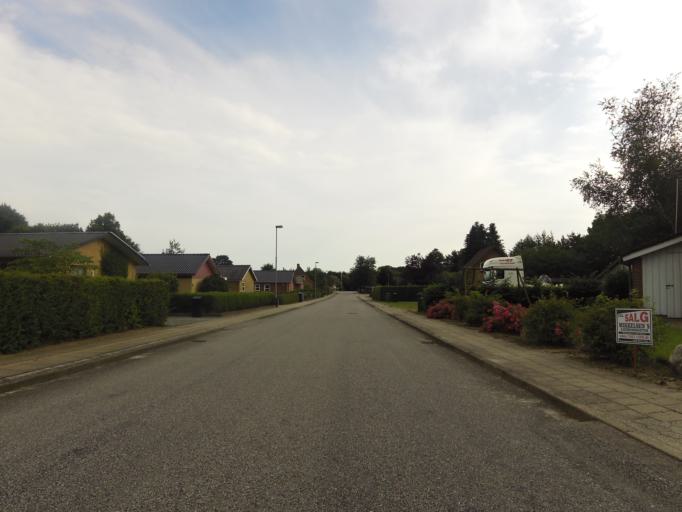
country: DK
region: South Denmark
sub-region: Tonder Kommune
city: Logumkloster
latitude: 55.1530
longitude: 8.9625
